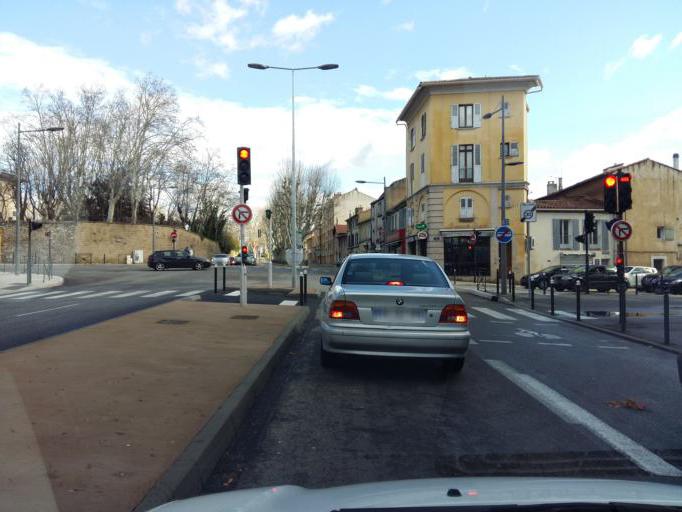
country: FR
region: Provence-Alpes-Cote d'Azur
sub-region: Departement des Bouches-du-Rhone
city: Aix-en-Provence
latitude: 43.5281
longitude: 5.4352
